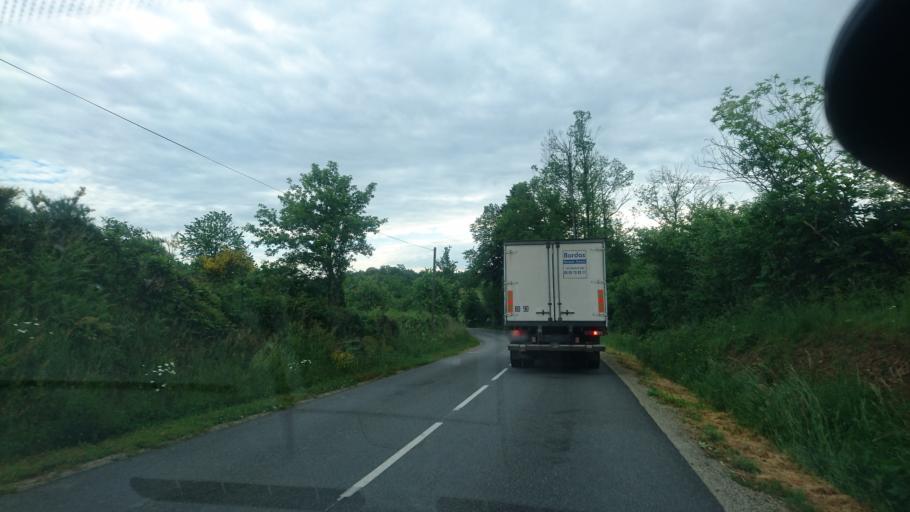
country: FR
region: Limousin
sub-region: Departement de la Haute-Vienne
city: Linards
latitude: 45.6565
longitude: 1.5565
